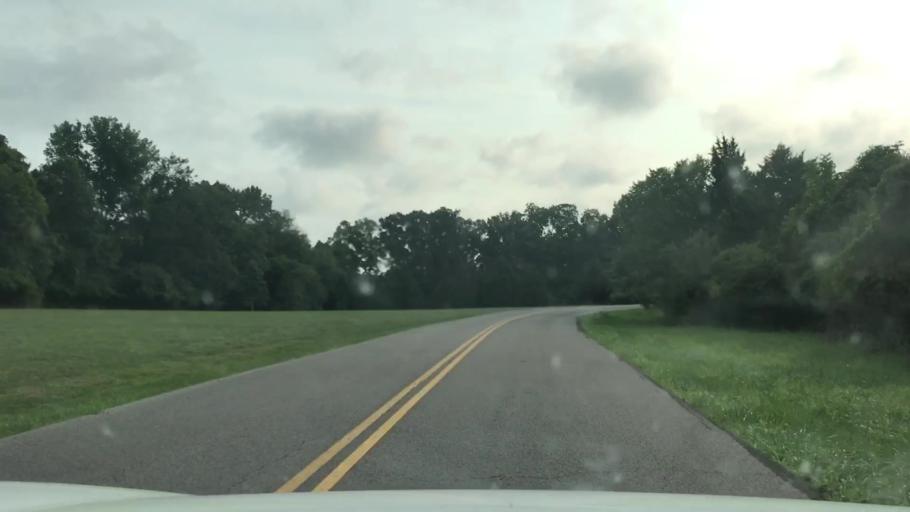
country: US
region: Missouri
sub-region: Saint Charles County
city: Weldon Spring
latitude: 38.7047
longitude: -90.6516
